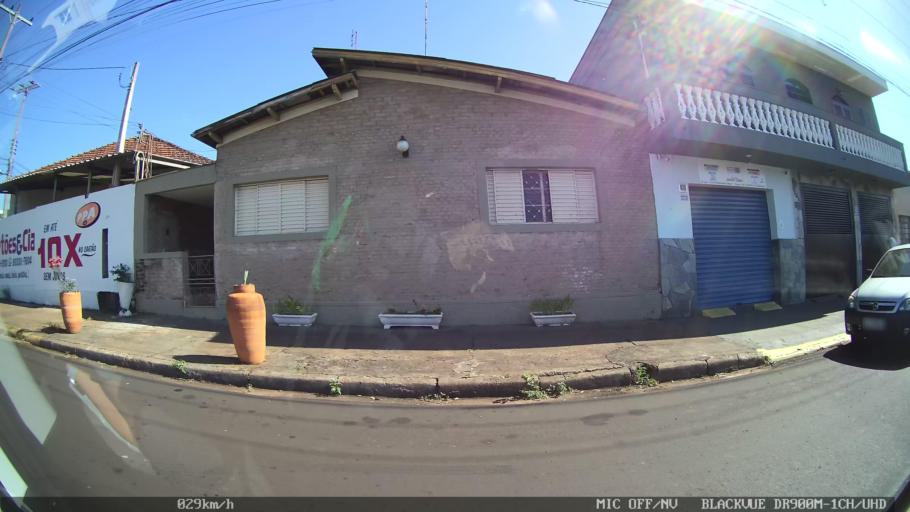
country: BR
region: Sao Paulo
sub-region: Batatais
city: Batatais
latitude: -20.8934
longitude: -47.5808
